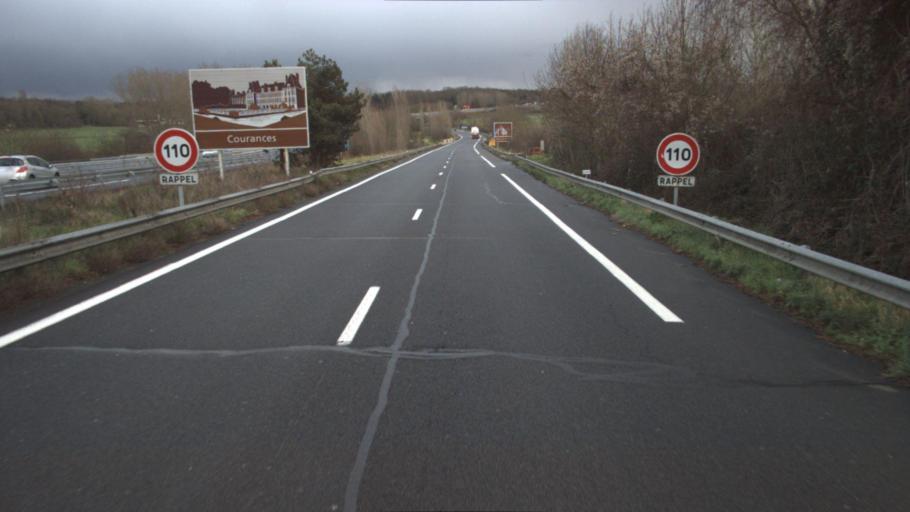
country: FR
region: Ile-de-France
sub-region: Departement de l'Essonne
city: Soisy-sur-Ecole
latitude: 48.4795
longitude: 2.5145
